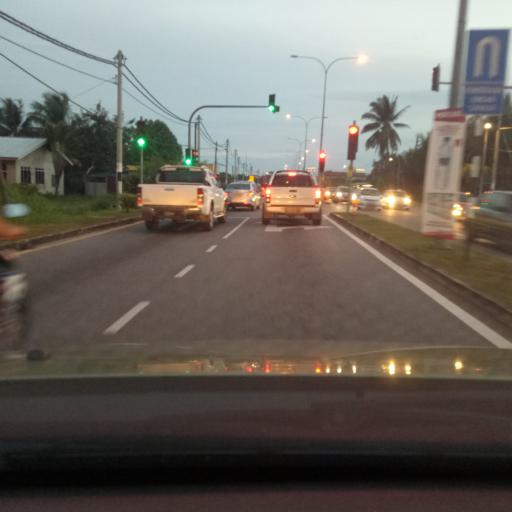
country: MY
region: Kedah
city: Alor Setar
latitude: 6.1074
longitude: 100.3727
